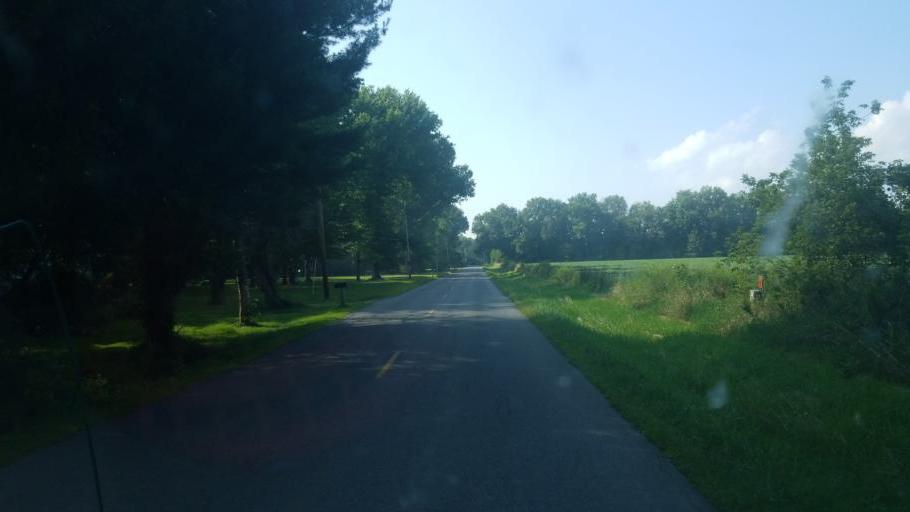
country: US
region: Ohio
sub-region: Medina County
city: Lodi
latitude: 41.0154
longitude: -82.0371
